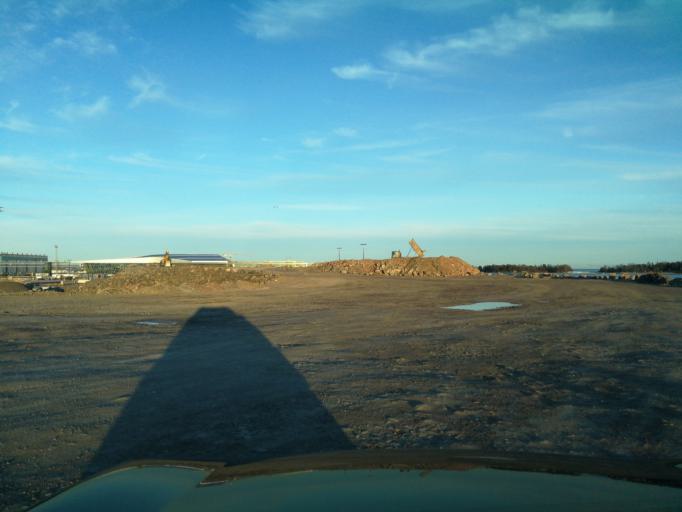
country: FI
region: Uusimaa
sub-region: Helsinki
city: Helsinki
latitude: 60.1513
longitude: 24.9046
